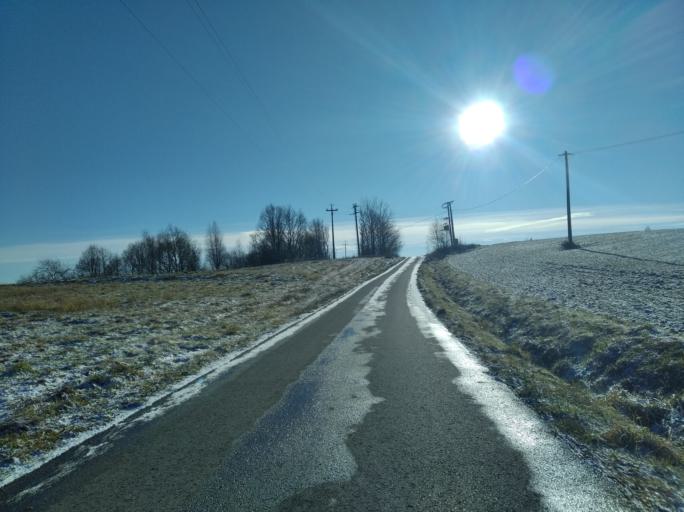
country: PL
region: Subcarpathian Voivodeship
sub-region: Powiat strzyzowski
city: Czudec
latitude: 49.9436
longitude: 21.7668
